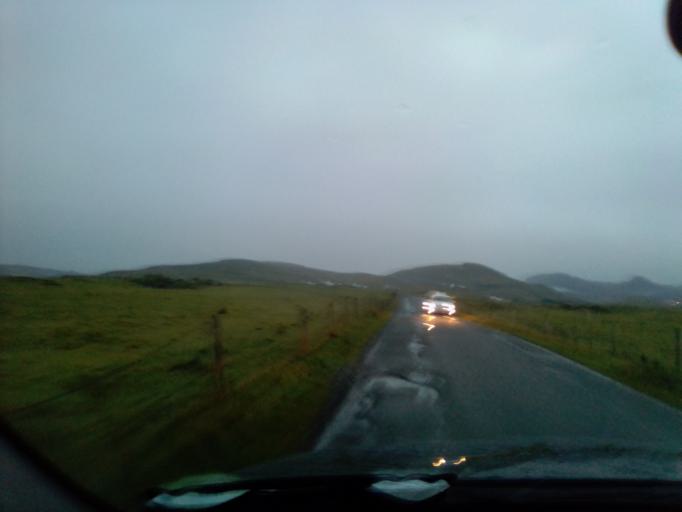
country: IE
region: Ulster
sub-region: County Donegal
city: Ramelton
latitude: 55.2602
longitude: -7.6828
